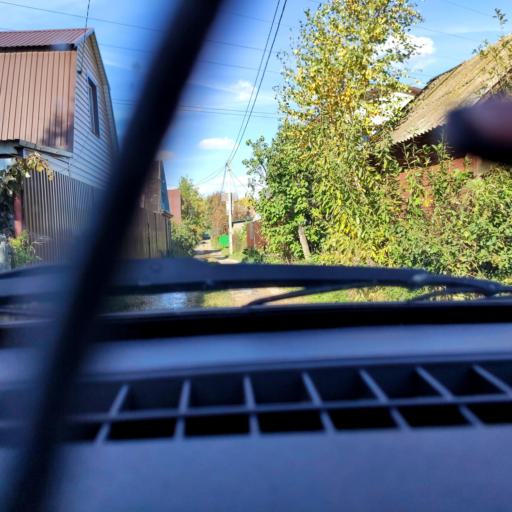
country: RU
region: Bashkortostan
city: Iglino
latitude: 54.7781
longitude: 56.2089
